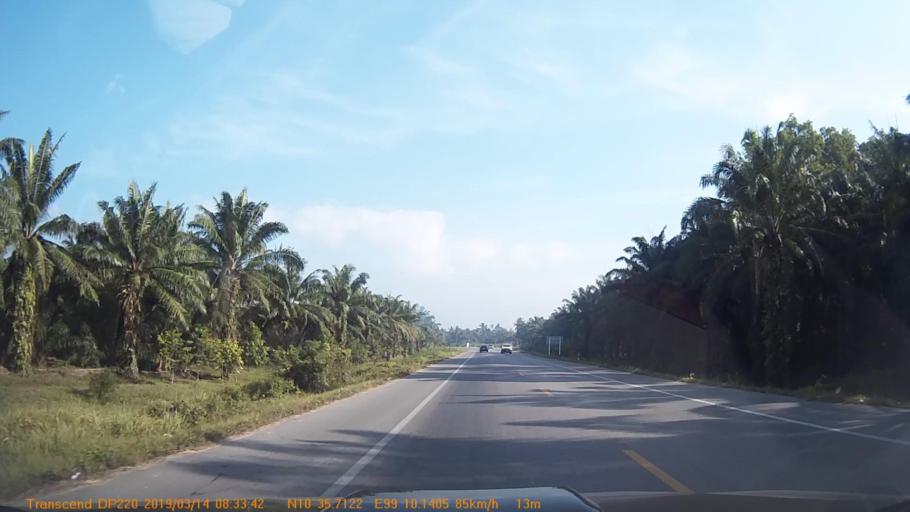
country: TH
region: Chumphon
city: Tha Sae
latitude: 10.5956
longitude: 99.1690
